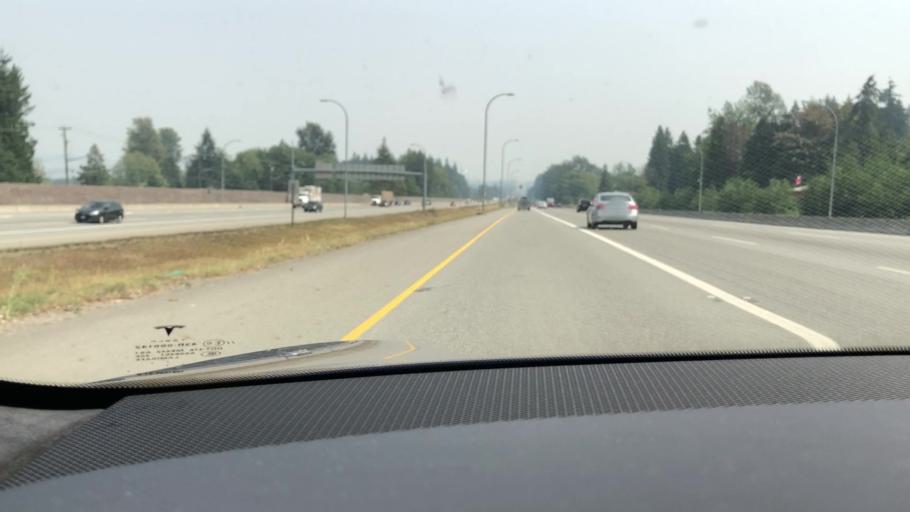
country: CA
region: British Columbia
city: Pitt Meadows
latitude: 49.1805
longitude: -122.7311
